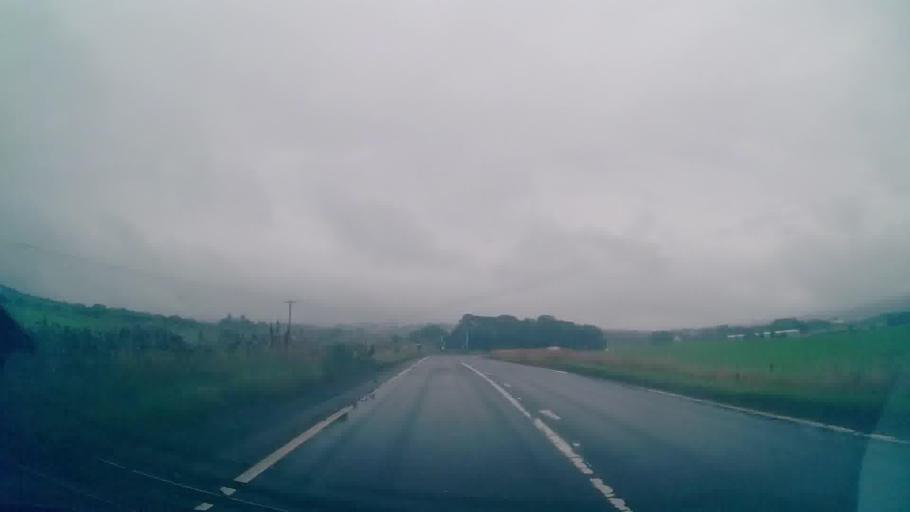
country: GB
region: Scotland
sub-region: Dumfries and Galloway
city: Sanquhar
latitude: 55.3781
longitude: -3.9436
